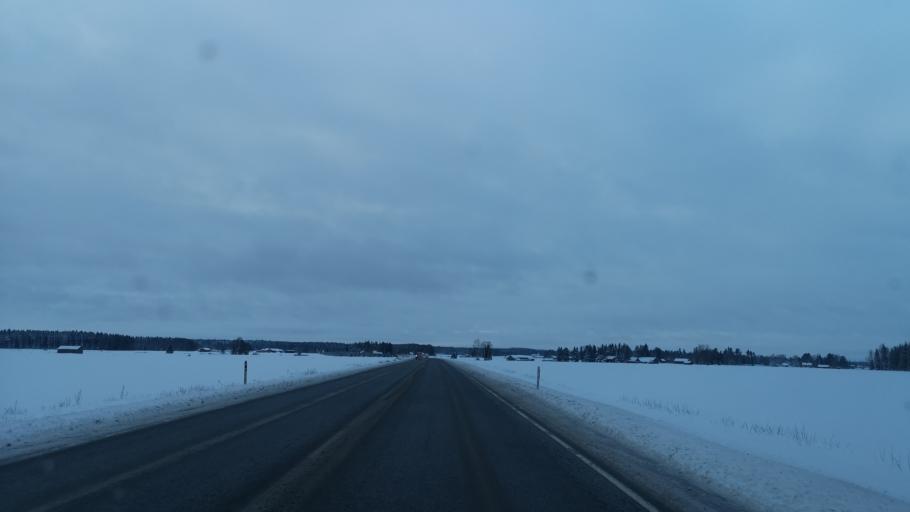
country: FI
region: Varsinais-Suomi
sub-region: Loimaa
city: Loimaa
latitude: 60.8916
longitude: 23.1077
